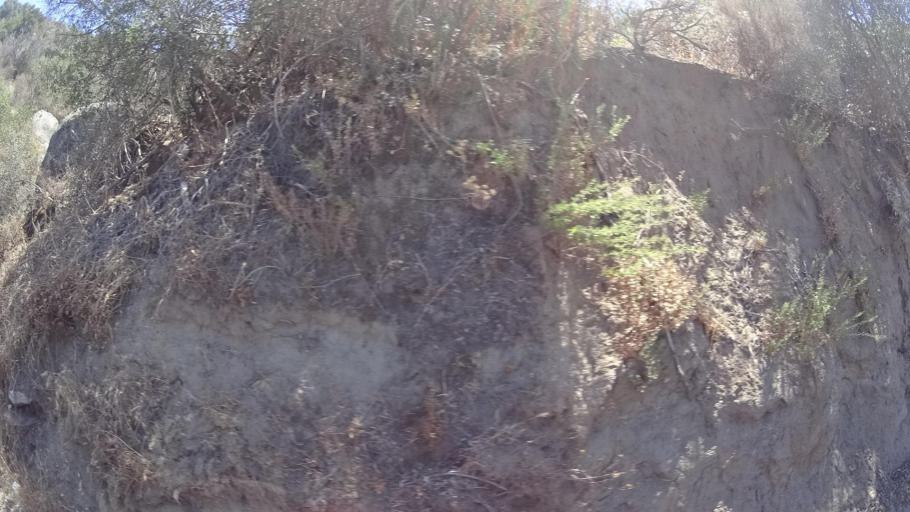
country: US
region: California
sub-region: San Diego County
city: Rainbow
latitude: 33.3464
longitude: -117.0799
